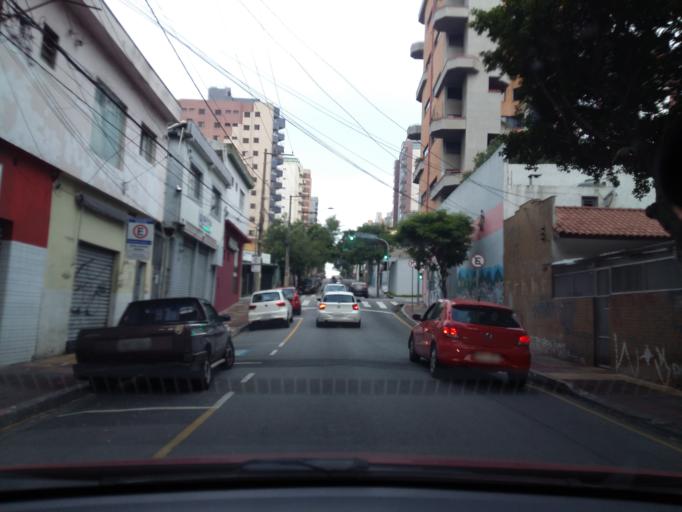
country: BR
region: Sao Paulo
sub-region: Sao Caetano Do Sul
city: Sao Caetano do Sul
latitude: -23.6191
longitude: -46.5672
